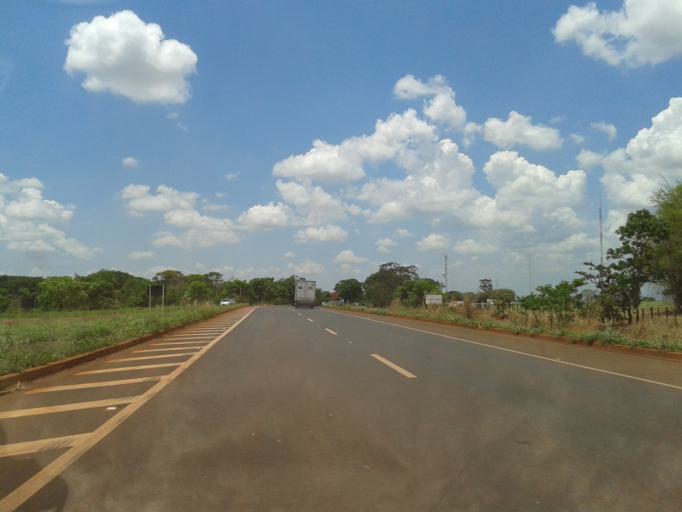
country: BR
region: Goias
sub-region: Itumbiara
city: Itumbiara
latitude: -18.3845
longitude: -49.3436
